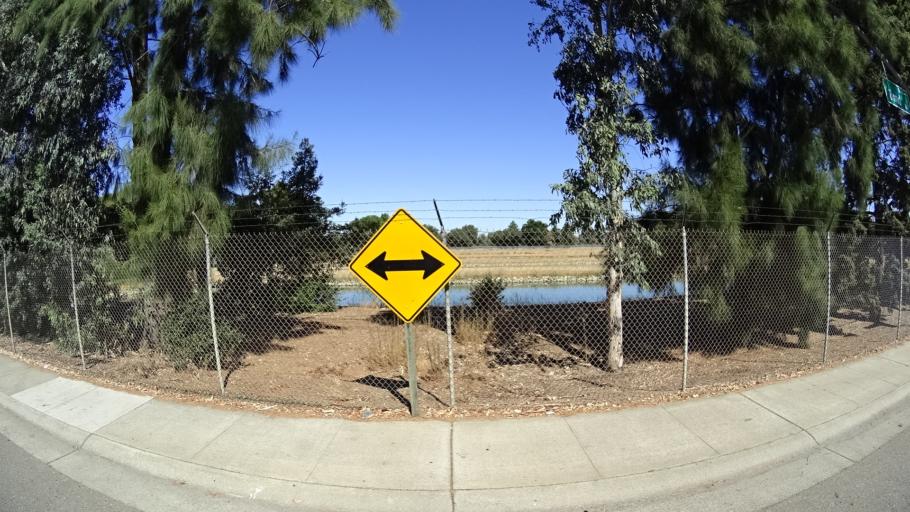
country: US
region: California
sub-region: Sacramento County
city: Elk Grove
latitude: 38.4235
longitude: -121.3849
